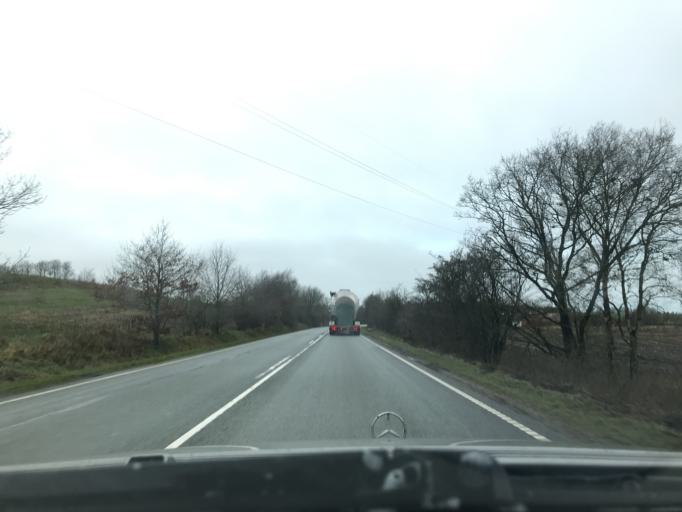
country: DK
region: South Denmark
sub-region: Esbjerg Kommune
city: Ribe
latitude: 55.2688
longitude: 8.8784
